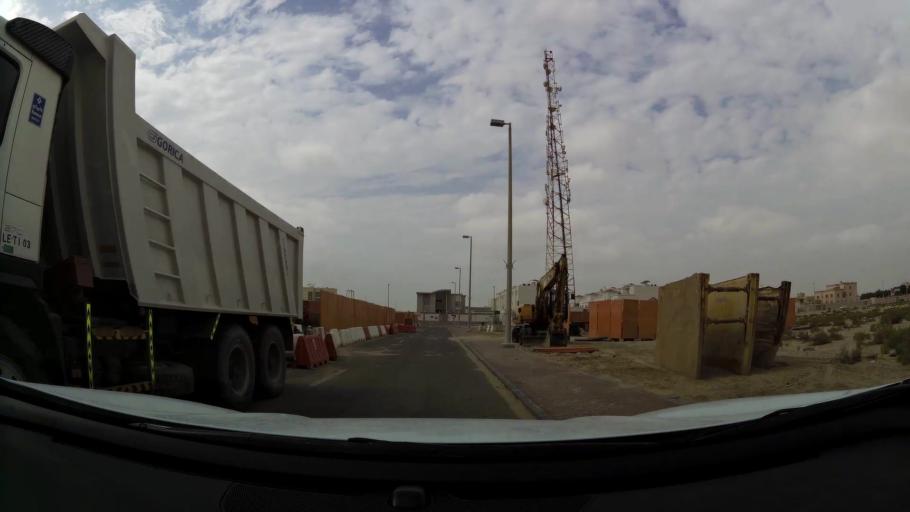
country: AE
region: Abu Dhabi
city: Abu Dhabi
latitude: 24.3832
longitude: 54.6390
